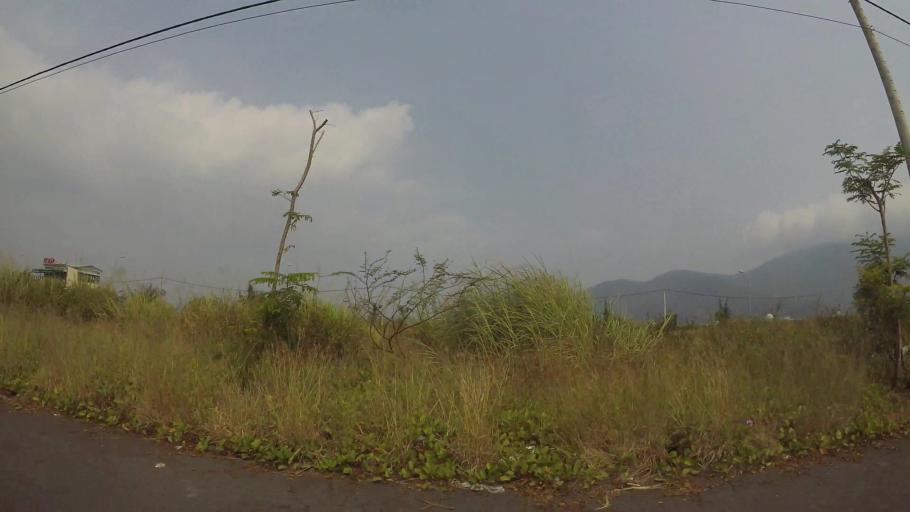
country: VN
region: Da Nang
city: Da Nang
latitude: 16.1026
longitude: 108.2332
